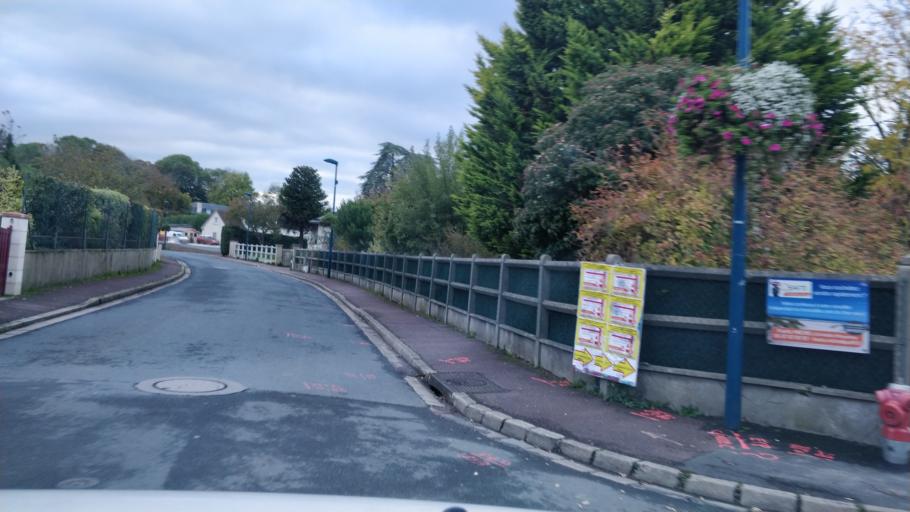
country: FR
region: Lower Normandy
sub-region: Departement du Calvados
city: Colleville-Montgomery
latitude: 49.2625
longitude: -0.2860
